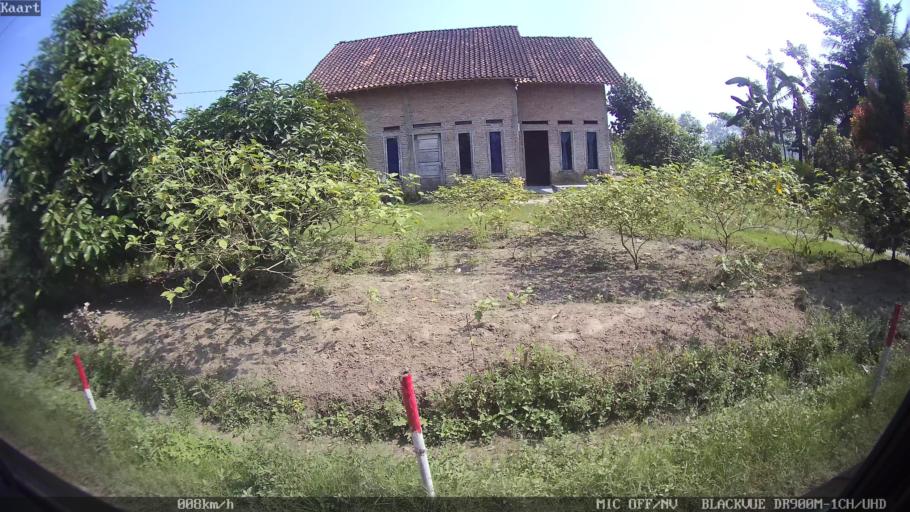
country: ID
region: Lampung
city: Natar
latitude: -5.2641
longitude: 105.2122
